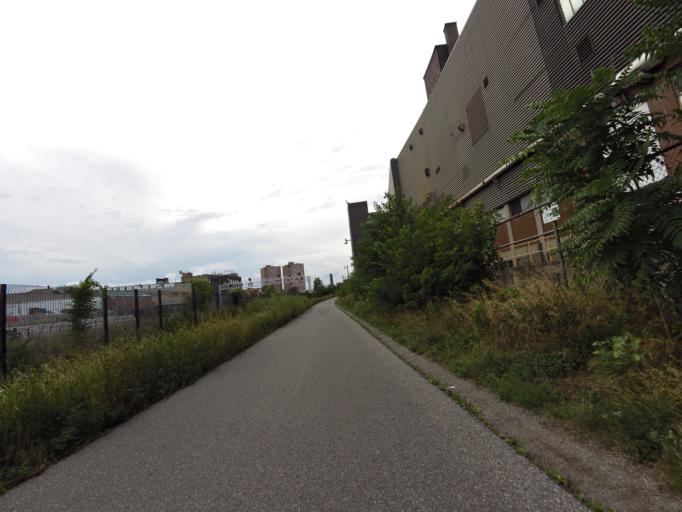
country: CA
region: Ontario
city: Toronto
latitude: 43.6518
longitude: -79.4446
